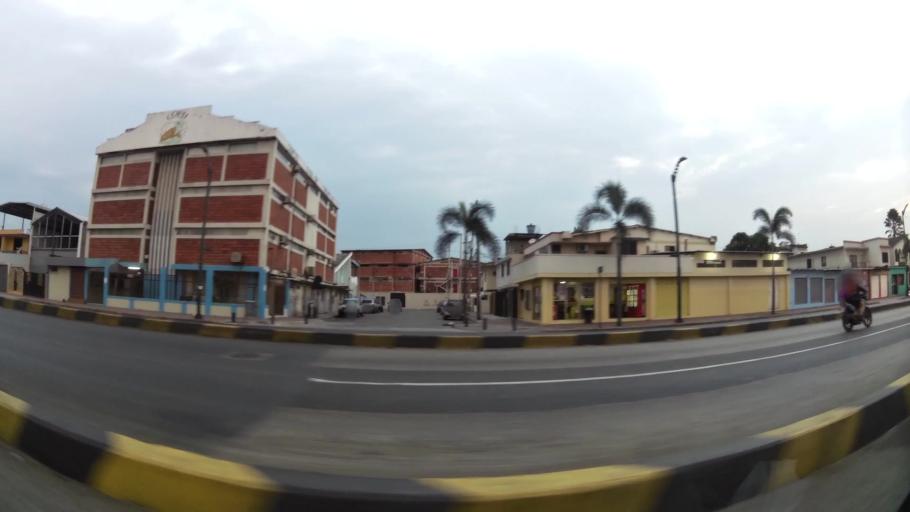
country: EC
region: Guayas
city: Guayaquil
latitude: -2.1792
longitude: -79.8902
